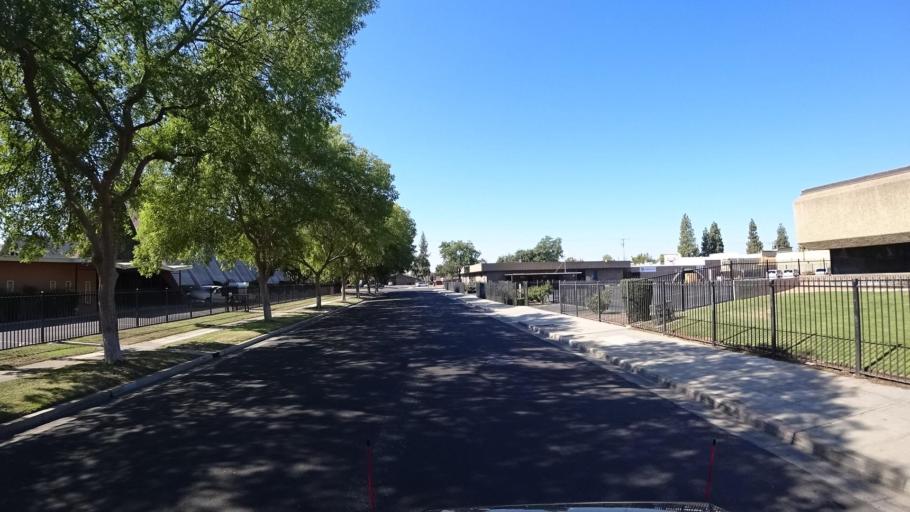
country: US
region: California
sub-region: Fresno County
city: Fresno
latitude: 36.7806
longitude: -119.7681
